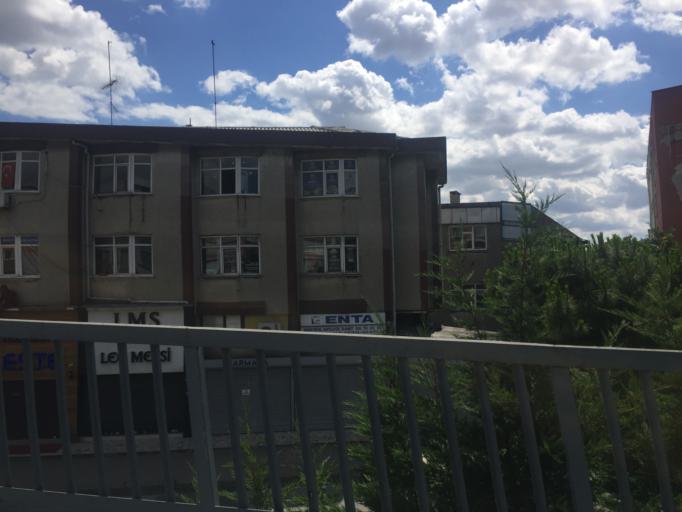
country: TR
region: Istanbul
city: merter keresteciler
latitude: 41.0311
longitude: 28.9146
